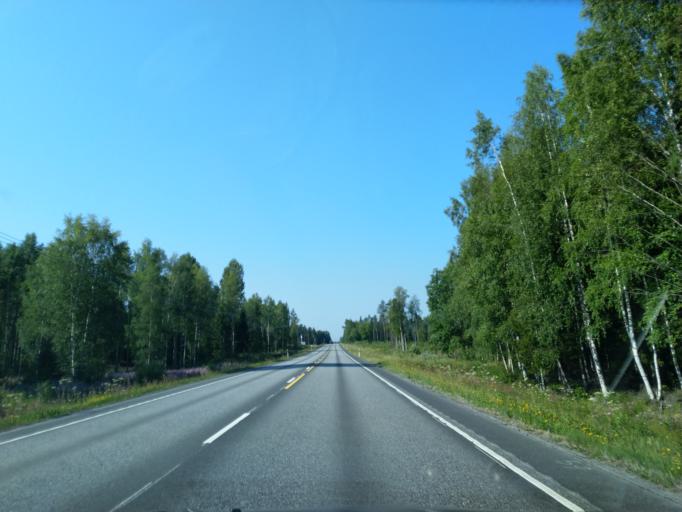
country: FI
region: Satakunta
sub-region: Pori
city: Pomarkku
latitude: 61.7313
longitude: 22.0729
